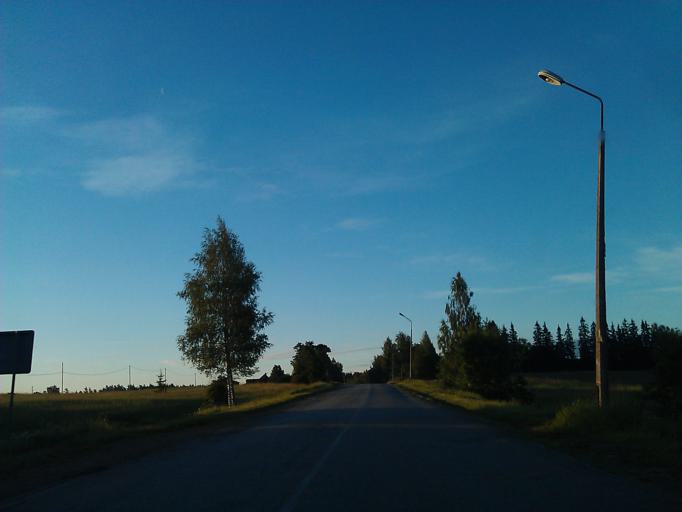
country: LV
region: Pargaujas
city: Stalbe
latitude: 57.3362
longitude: 25.1514
